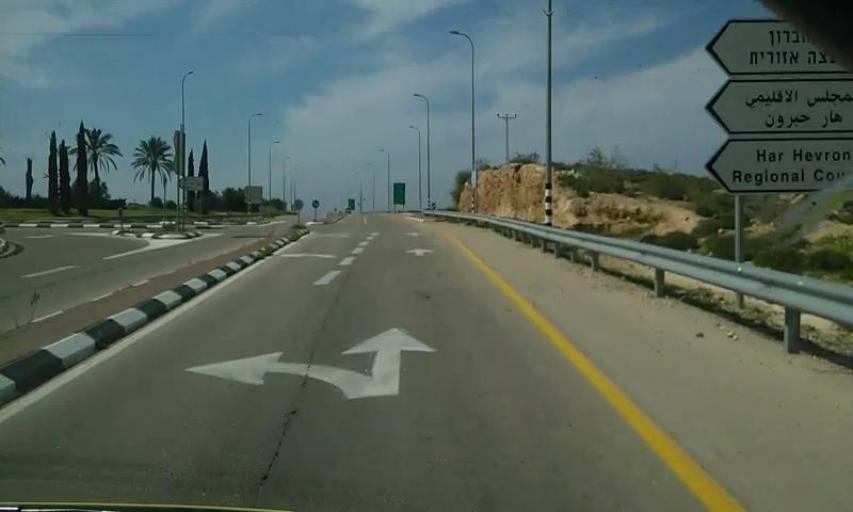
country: PS
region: West Bank
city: Az Zahiriyah
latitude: 31.3758
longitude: 35.0074
